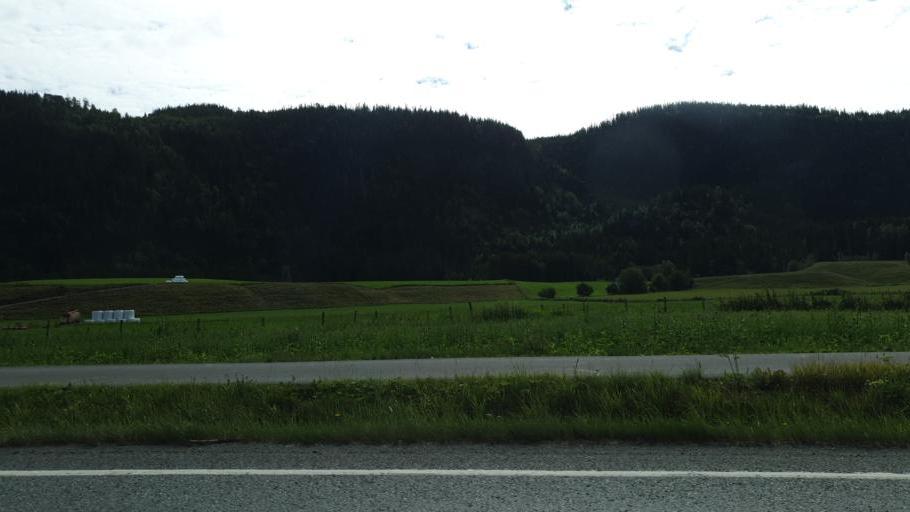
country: NO
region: Sor-Trondelag
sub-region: Melhus
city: Lundamo
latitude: 63.1664
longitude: 10.3116
